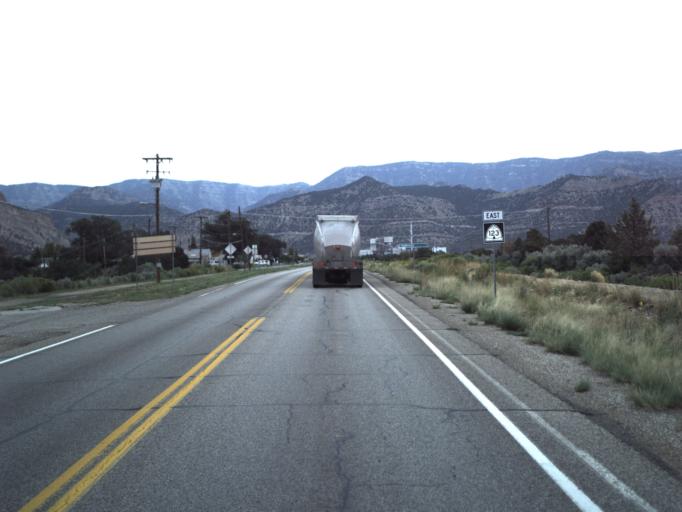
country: US
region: Utah
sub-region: Carbon County
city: East Carbon City
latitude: 39.5433
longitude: -110.4138
